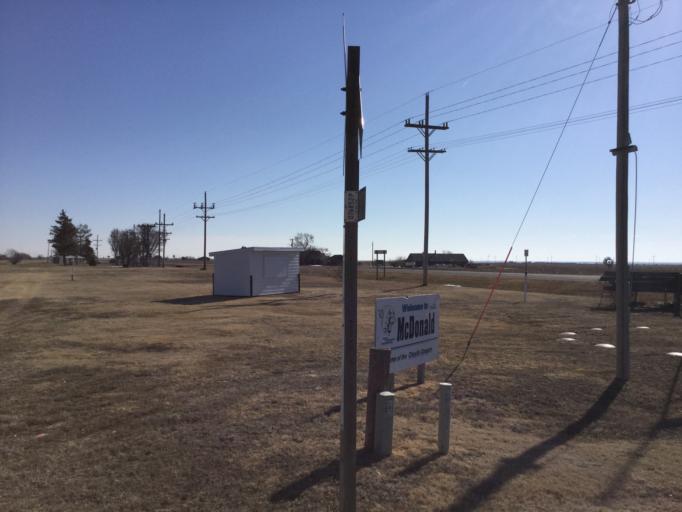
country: US
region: Nebraska
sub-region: Dundy County
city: Benkelman
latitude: 39.7819
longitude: -101.3726
